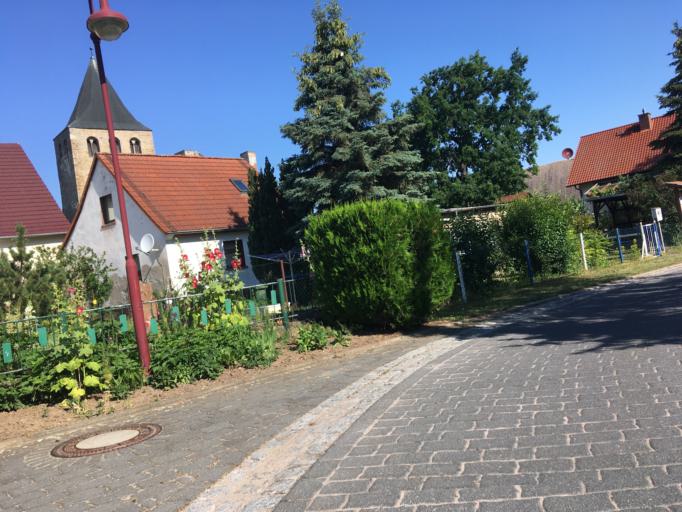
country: DE
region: Saxony-Anhalt
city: Koethen
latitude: 51.7605
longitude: 11.9364
